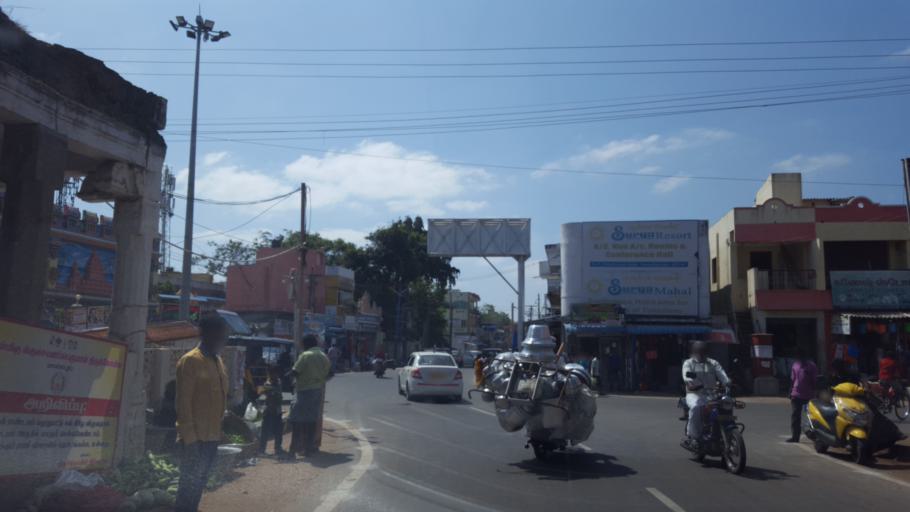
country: IN
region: Tamil Nadu
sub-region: Kancheepuram
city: Mamallapuram
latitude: 12.6211
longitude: 80.1945
